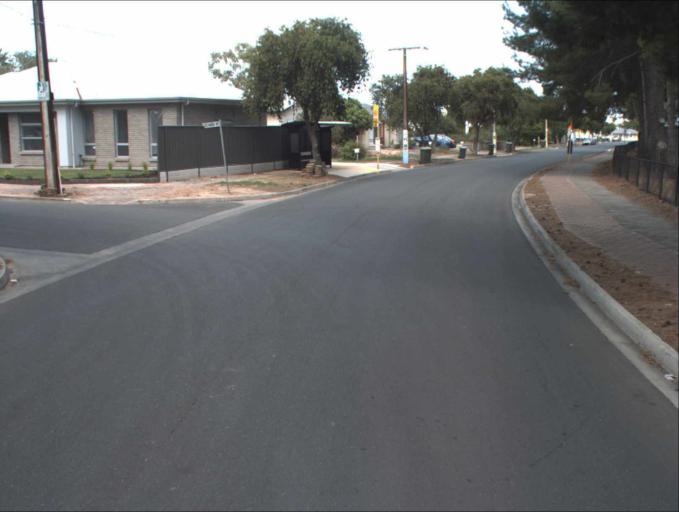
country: AU
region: South Australia
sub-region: Campbelltown
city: Paradise
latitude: -34.8614
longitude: 138.6602
